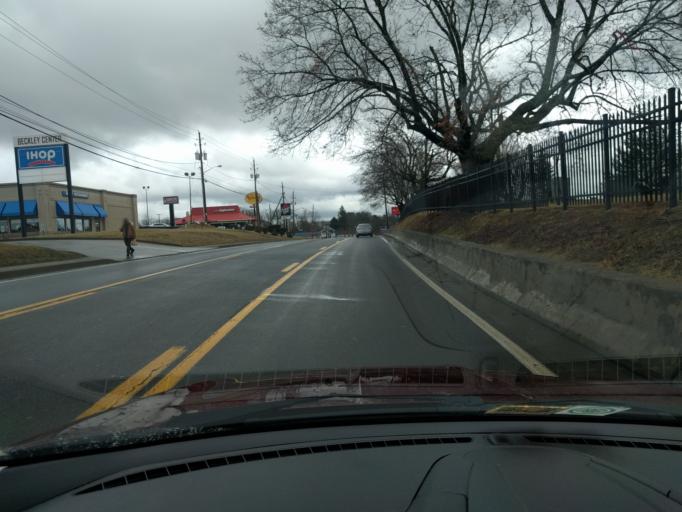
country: US
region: West Virginia
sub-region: Raleigh County
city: Mabscott
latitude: 37.7909
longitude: -81.2121
